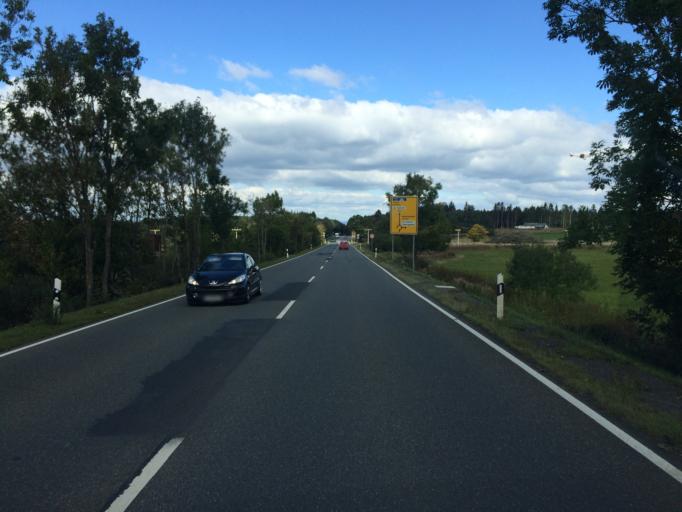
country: DE
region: Rheinland-Pfalz
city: Liebenscheid
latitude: 50.7123
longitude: 8.0696
